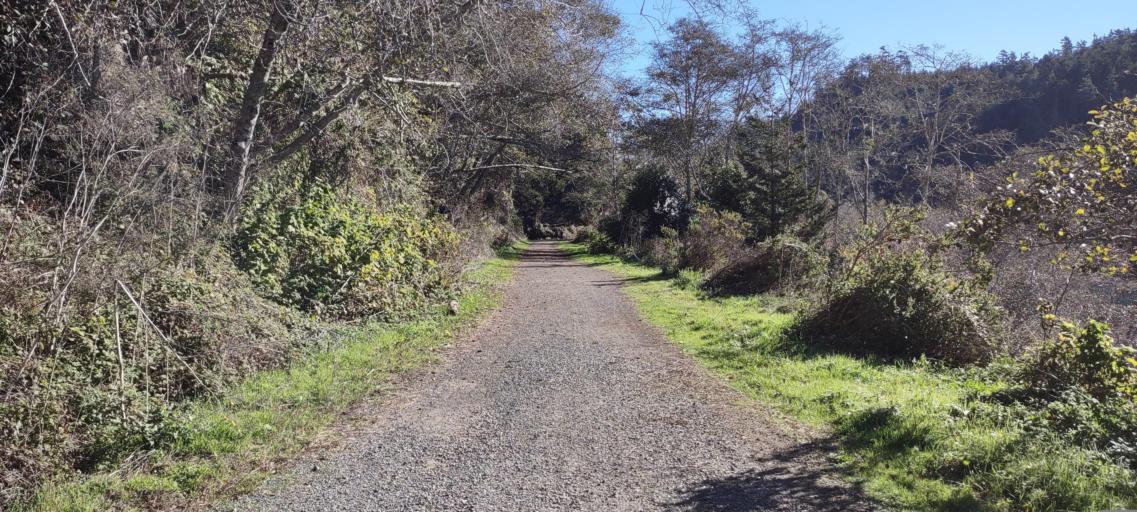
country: US
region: California
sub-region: Mendocino County
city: Fort Bragg
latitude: 39.3050
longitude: -123.7777
